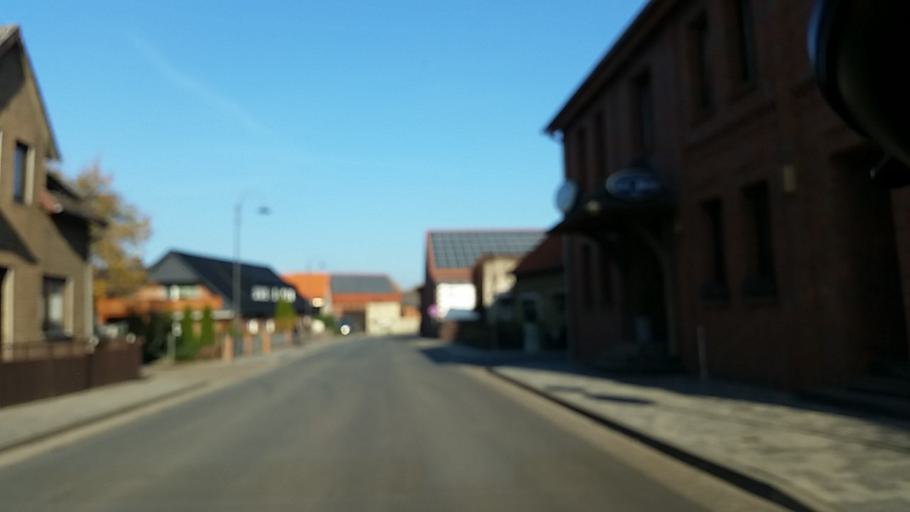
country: DE
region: Lower Saxony
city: Bergfeld
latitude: 52.5448
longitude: 10.8453
